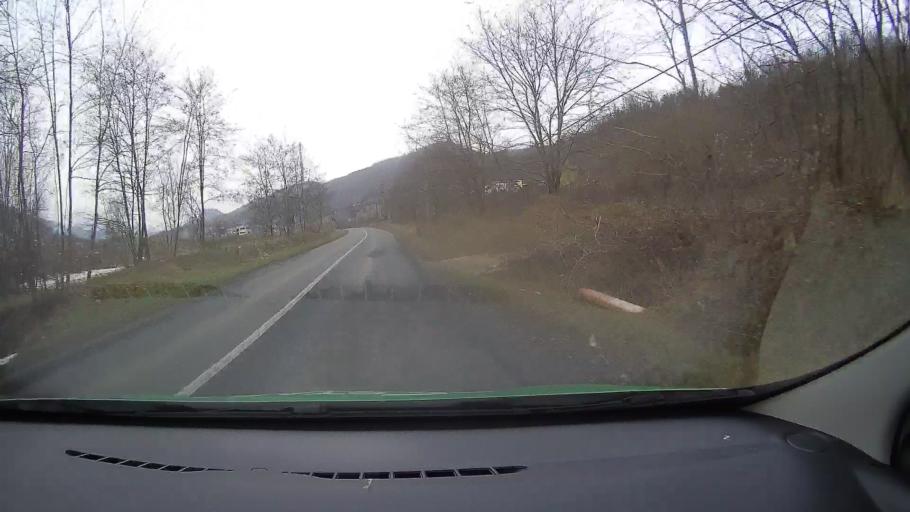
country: RO
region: Alba
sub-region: Oras Zlatna
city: Zlatna
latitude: 46.0977
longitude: 23.2533
